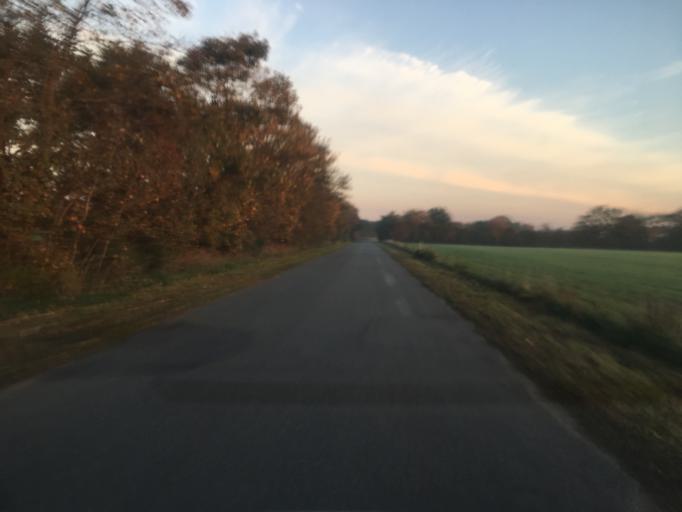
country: DK
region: South Denmark
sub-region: Tonder Kommune
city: Logumkloster
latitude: 55.0182
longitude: 9.0462
